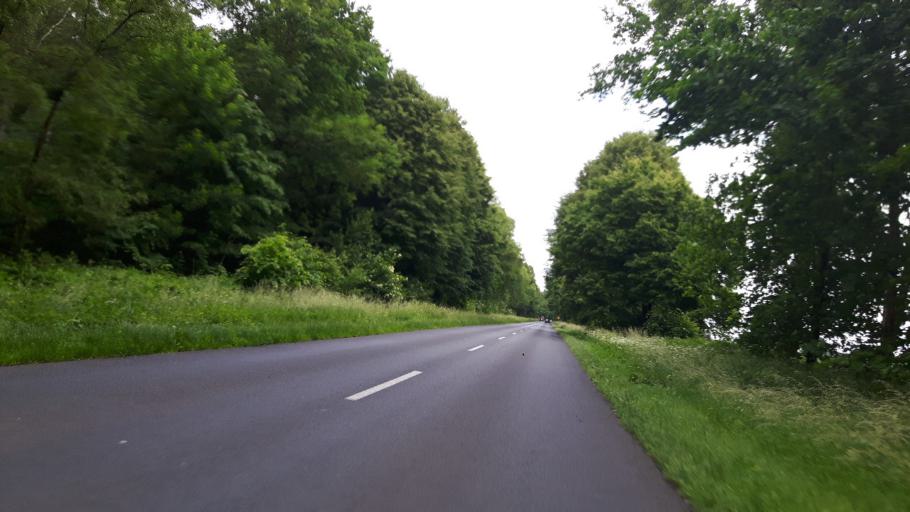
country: PL
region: West Pomeranian Voivodeship
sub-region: Powiat gryficki
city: Trzebiatow
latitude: 53.9938
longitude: 15.2396
